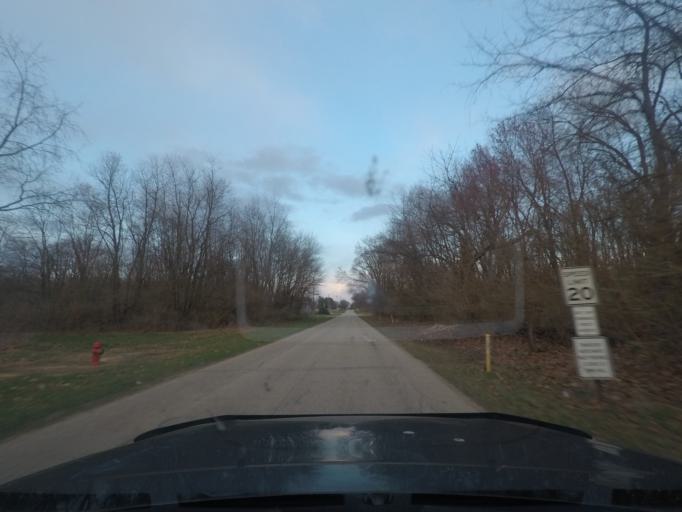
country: US
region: Indiana
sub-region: LaPorte County
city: Kingsford Heights
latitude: 41.4765
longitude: -86.6992
